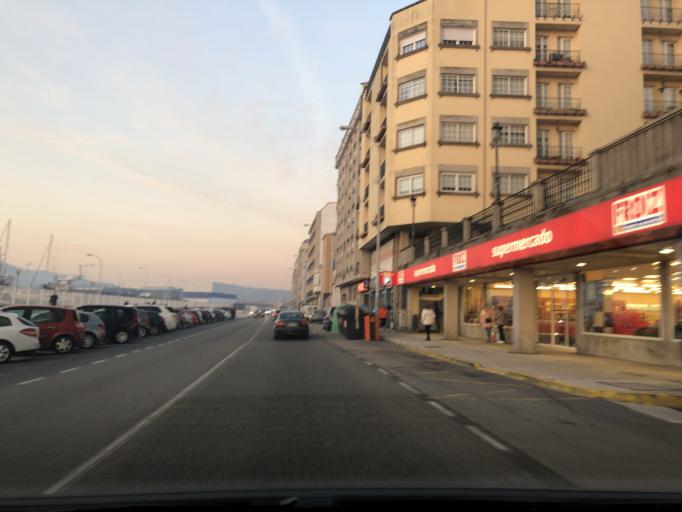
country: ES
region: Galicia
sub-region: Provincia de Pontevedra
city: Marin
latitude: 42.3951
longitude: -8.6934
